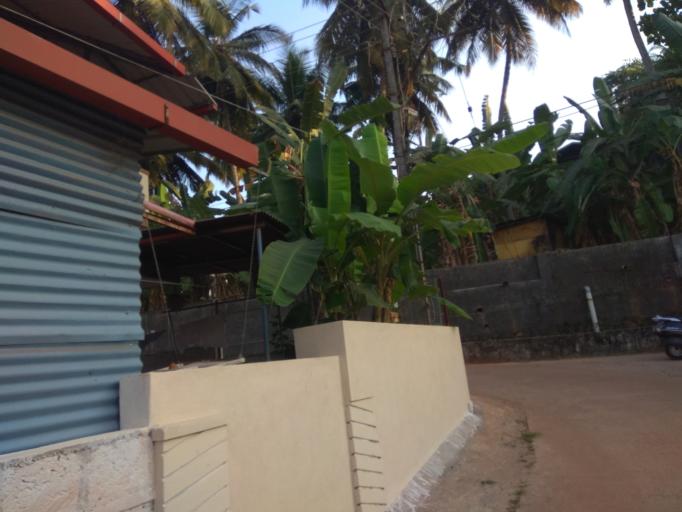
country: IN
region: Karnataka
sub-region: Dakshina Kannada
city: Mangalore
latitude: 12.8933
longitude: 74.8540
